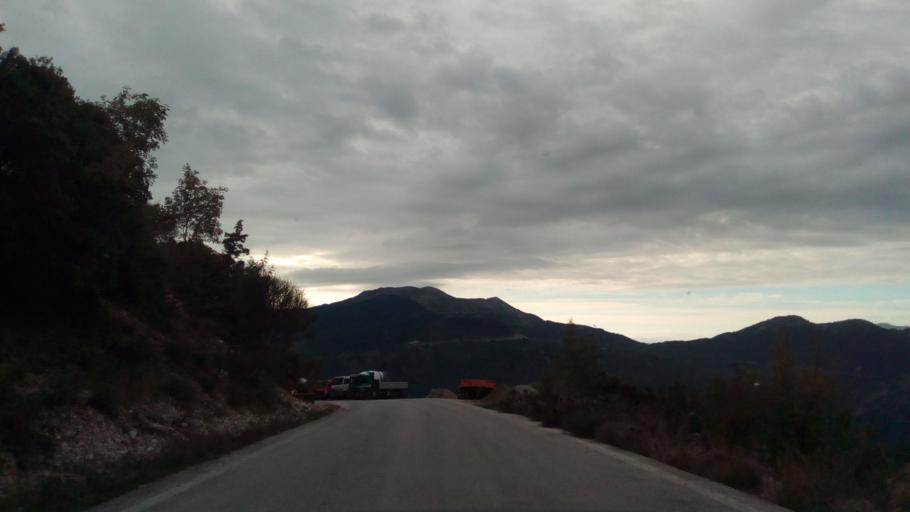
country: GR
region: West Greece
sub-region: Nomos Aitolias kai Akarnanias
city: Thermo
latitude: 38.6026
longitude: 21.8041
